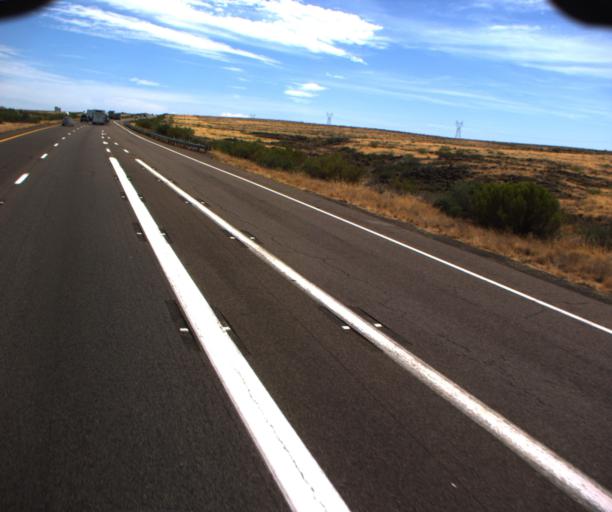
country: US
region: Arizona
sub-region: Yavapai County
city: Cordes Lakes
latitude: 34.1976
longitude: -112.1286
